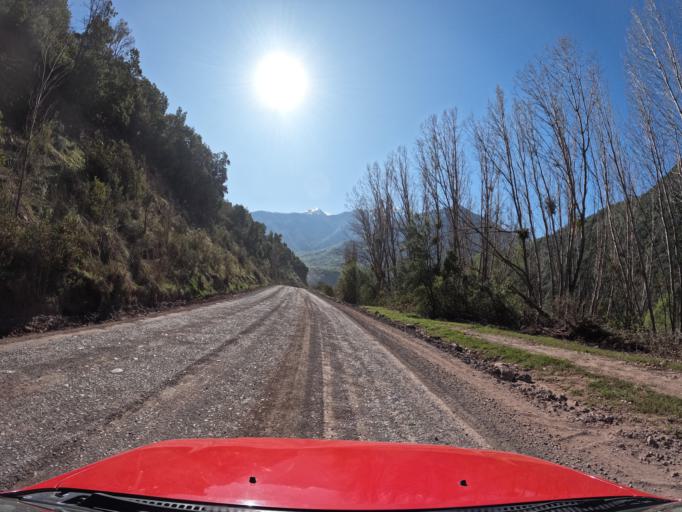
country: CL
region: O'Higgins
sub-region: Provincia de Colchagua
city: Chimbarongo
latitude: -35.0044
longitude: -70.7586
